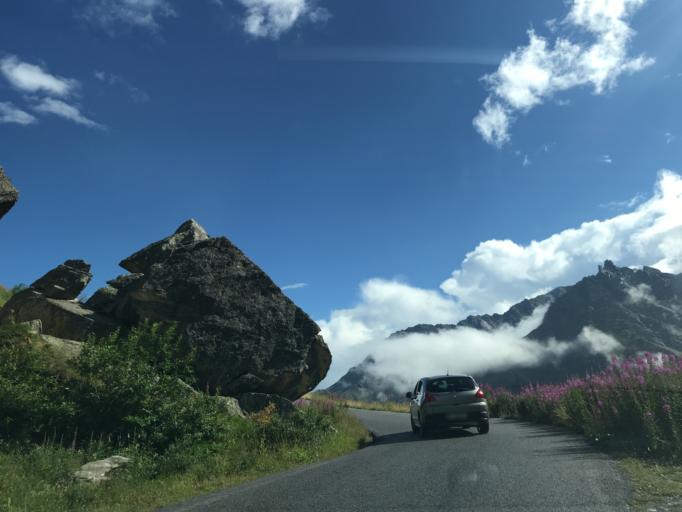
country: IT
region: Piedmont
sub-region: Provincia di Cuneo
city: Pontechianale
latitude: 44.6626
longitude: 6.9865
